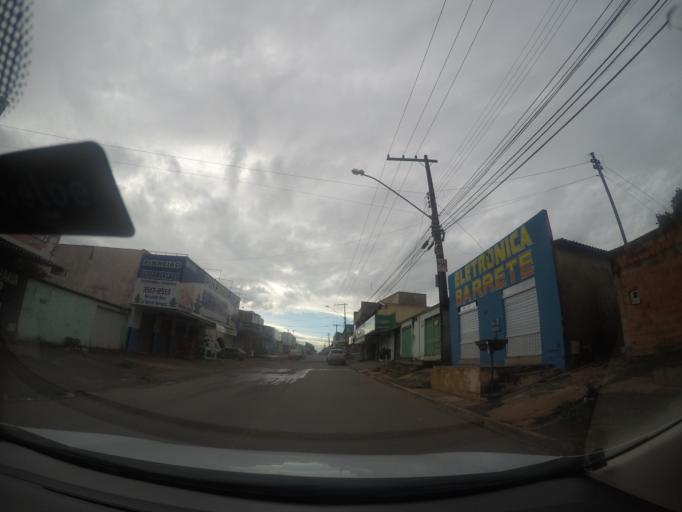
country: BR
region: Goias
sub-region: Goiania
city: Goiania
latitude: -16.6028
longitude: -49.3247
